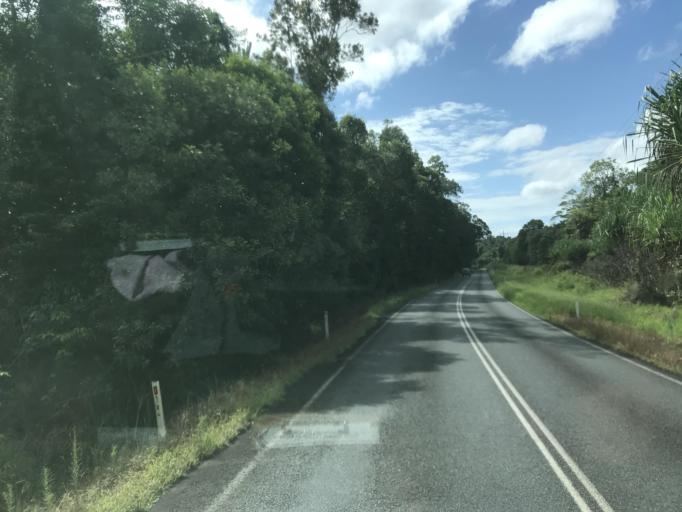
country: AU
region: Queensland
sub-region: Cassowary Coast
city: Innisfail
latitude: -17.8447
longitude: 146.0566
